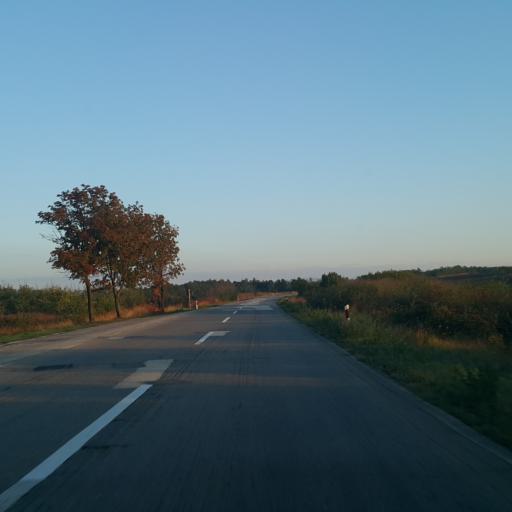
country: RS
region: Central Serbia
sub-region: Zajecarski Okrug
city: Zajecar
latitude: 44.0143
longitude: 22.3010
